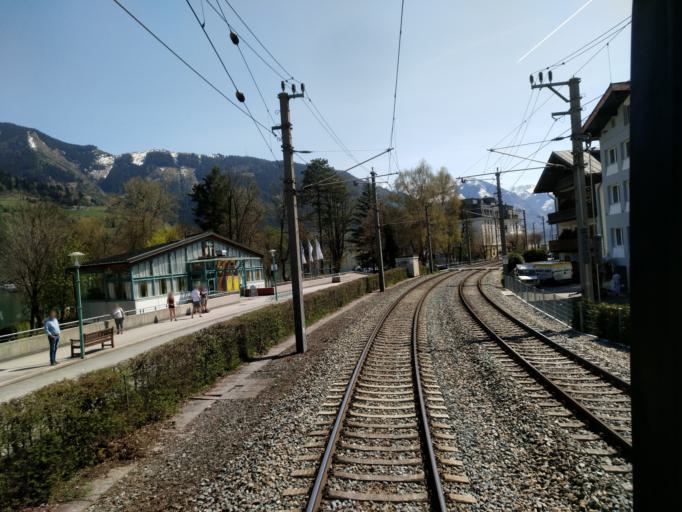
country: AT
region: Salzburg
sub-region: Politischer Bezirk Zell am See
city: Zell am See
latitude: 47.3262
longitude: 12.7997
